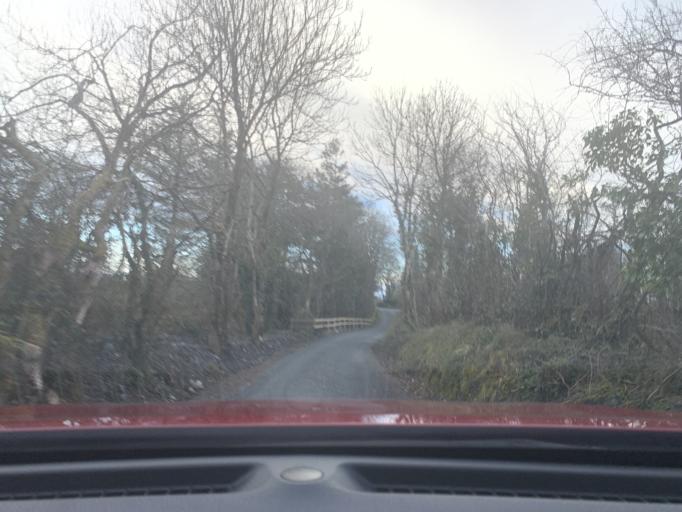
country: IE
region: Connaught
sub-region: Roscommon
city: Ballaghaderreen
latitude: 53.8955
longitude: -8.5876
